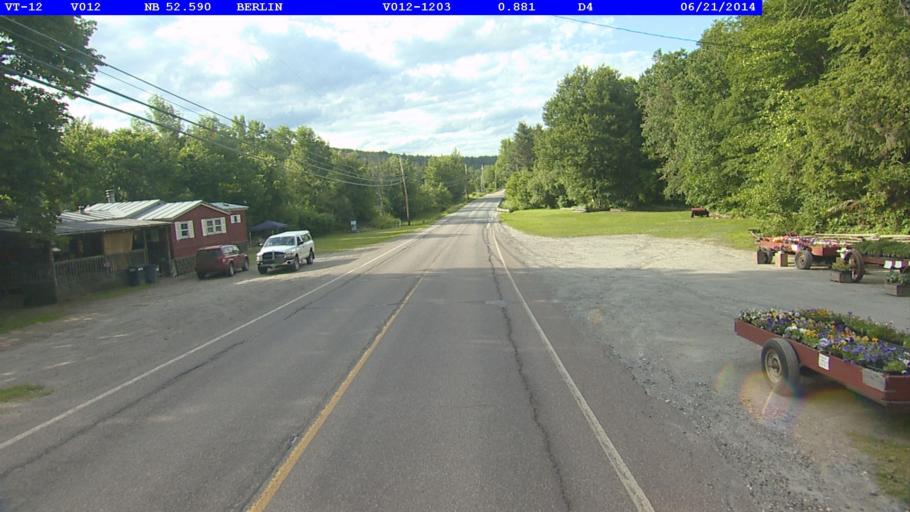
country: US
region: Vermont
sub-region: Washington County
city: Northfield
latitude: 44.1858
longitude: -72.6395
